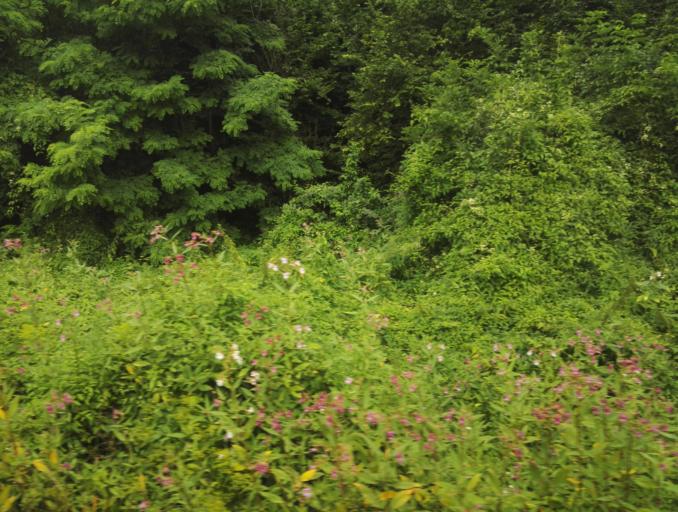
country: CH
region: Schaffhausen
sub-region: Bezirk Schleitheim
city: Schleitheim
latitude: 47.7716
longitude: 8.4810
